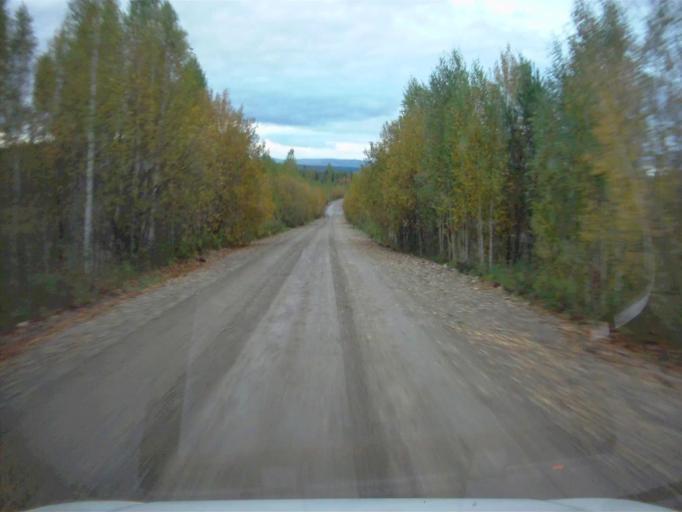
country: RU
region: Sverdlovsk
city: Mikhaylovsk
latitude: 56.2040
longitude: 59.2024
